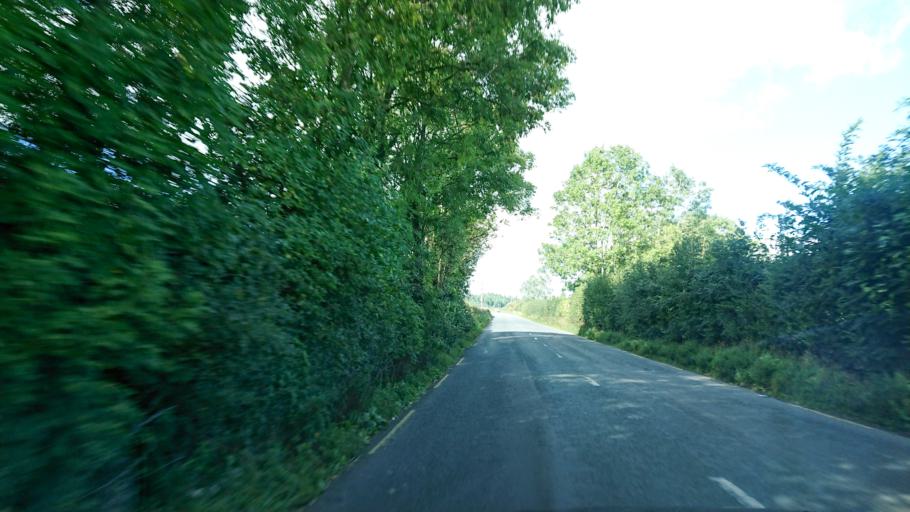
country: IE
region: Munster
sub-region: Waterford
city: Dungarvan
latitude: 52.1150
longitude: -7.6811
